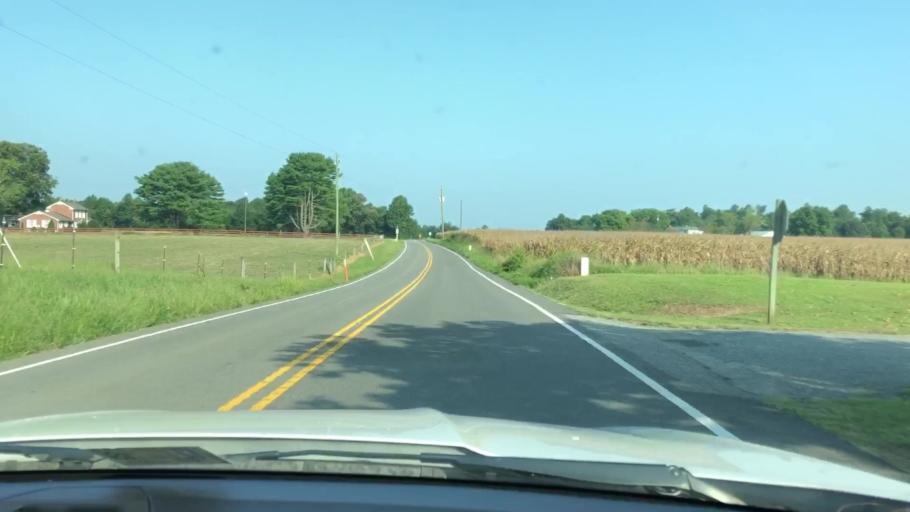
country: US
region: Virginia
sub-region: King William County
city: West Point
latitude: 37.6134
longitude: -76.7837
